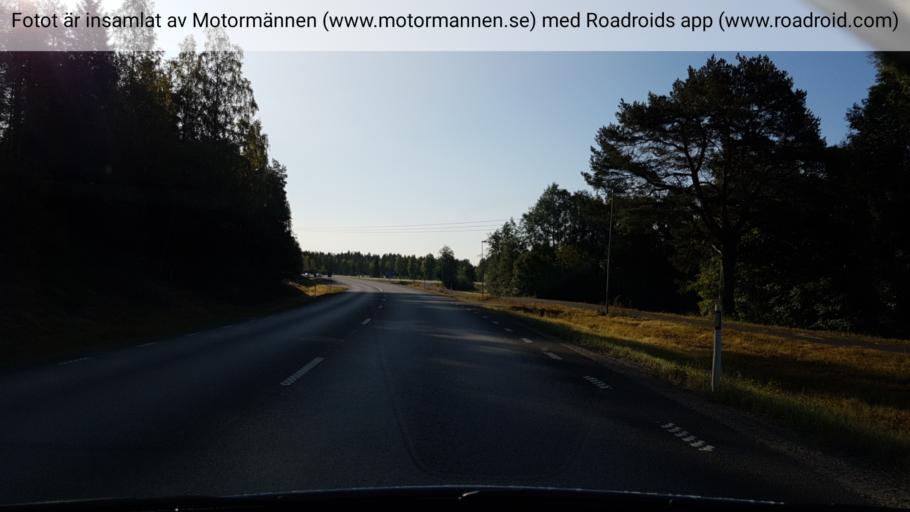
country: SE
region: Vaesterbotten
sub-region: Umea Kommun
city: Roback
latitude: 63.8566
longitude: 20.0950
